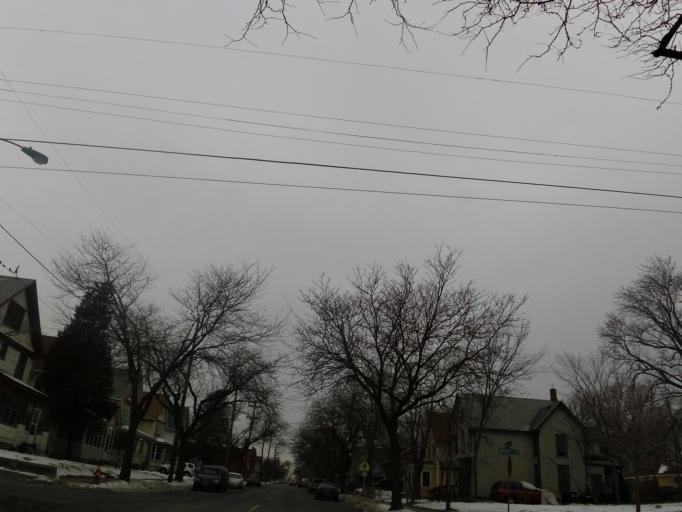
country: US
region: Minnesota
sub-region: Ramsey County
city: Saint Paul
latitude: 44.9535
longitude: -93.0689
